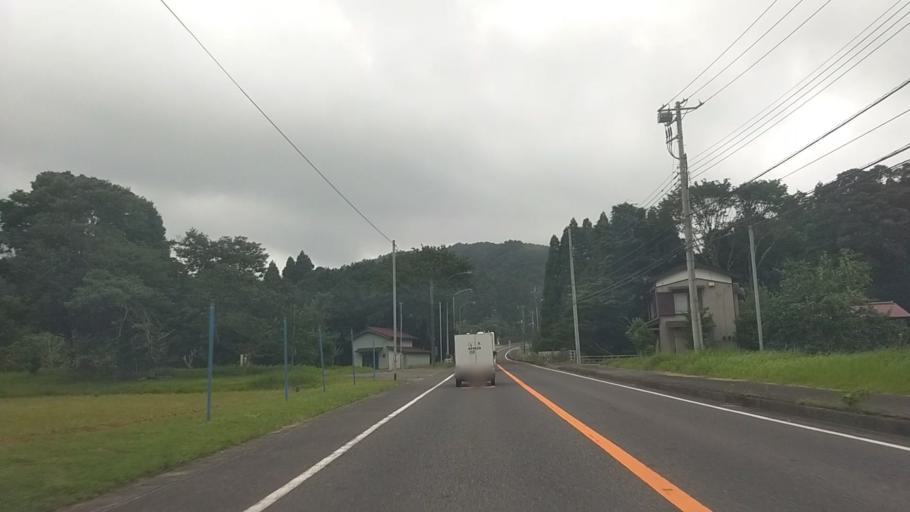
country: JP
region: Chiba
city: Kawaguchi
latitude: 35.1848
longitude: 140.0607
